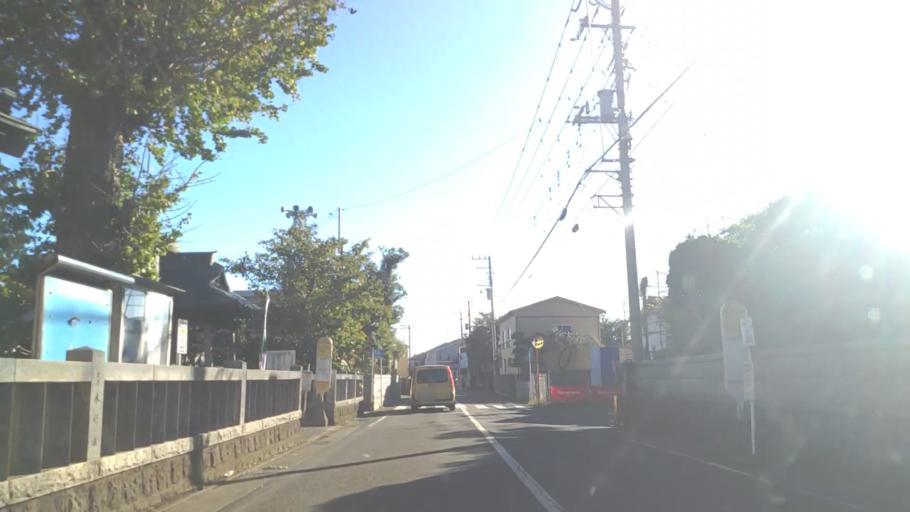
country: JP
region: Kanagawa
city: Atsugi
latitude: 35.3868
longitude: 139.3667
